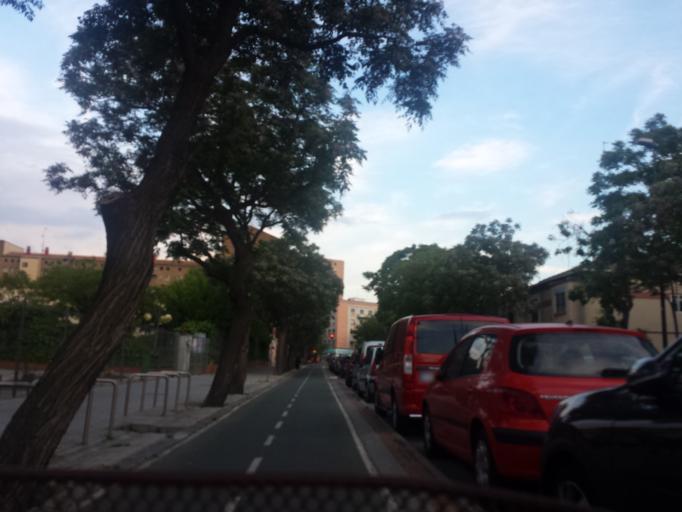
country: ES
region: Aragon
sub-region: Provincia de Zaragoza
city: Delicias
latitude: 41.6464
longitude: -0.9008
